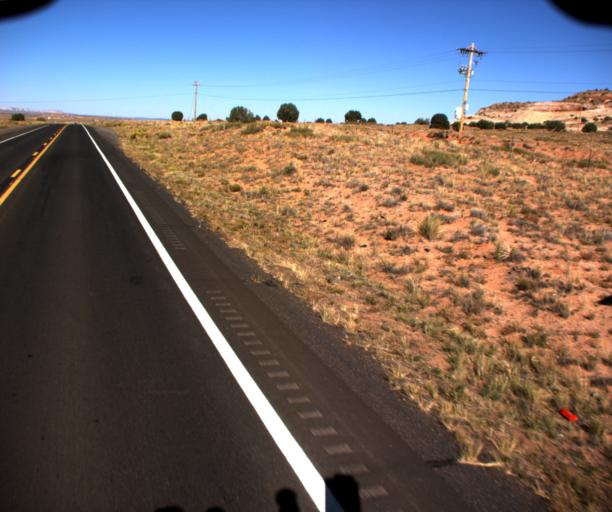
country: US
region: Arizona
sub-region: Coconino County
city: Tuba City
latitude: 36.2401
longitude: -111.0252
